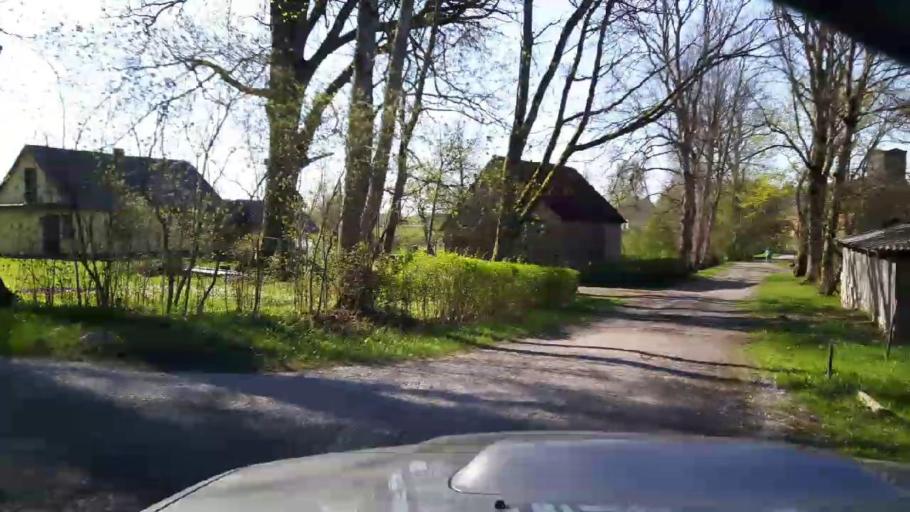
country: EE
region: Paernumaa
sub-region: Sindi linn
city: Sindi
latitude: 58.4487
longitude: 24.7639
